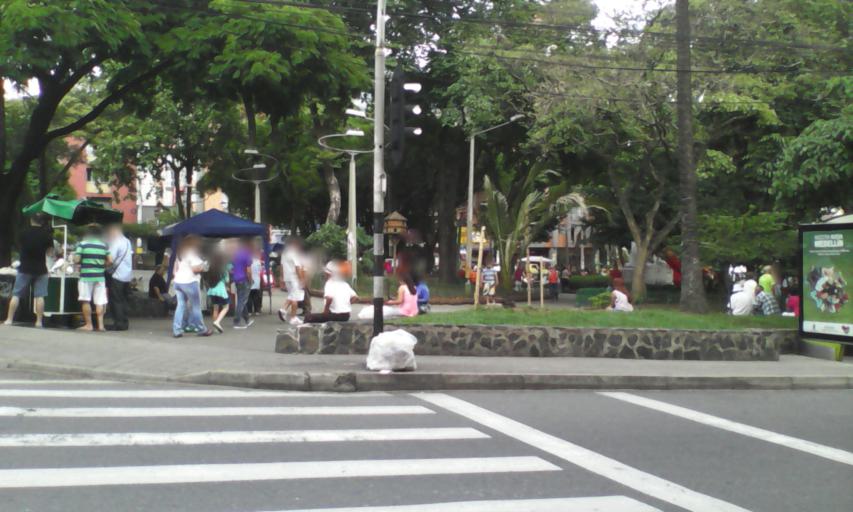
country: CO
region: Antioquia
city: Medellin
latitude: 6.2486
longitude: -75.5577
